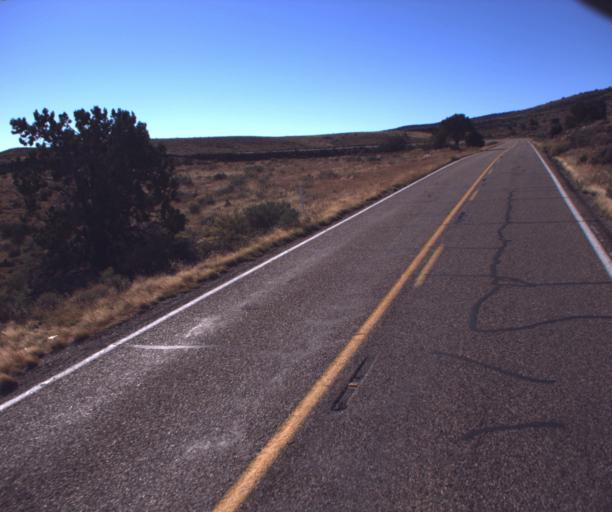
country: US
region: Arizona
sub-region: Coconino County
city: Fredonia
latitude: 36.7292
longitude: -112.0621
